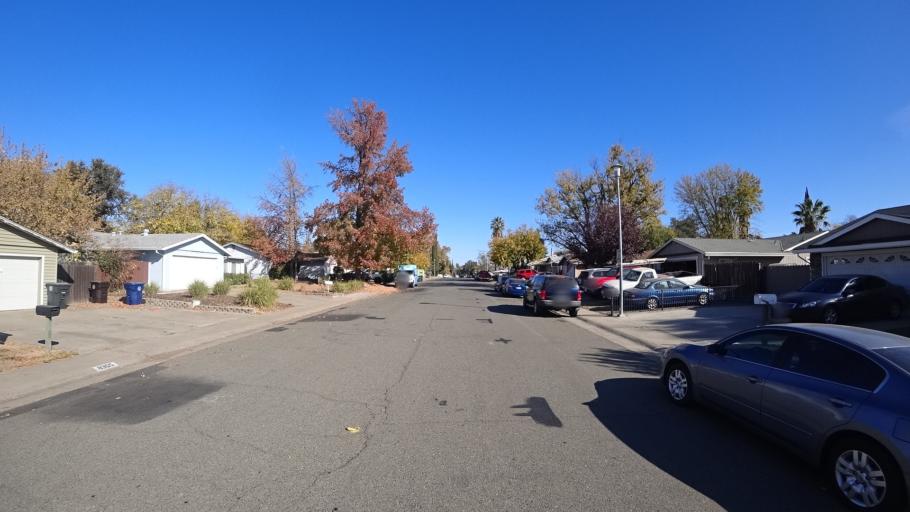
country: US
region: California
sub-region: Sacramento County
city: Antelope
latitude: 38.7167
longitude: -121.3148
